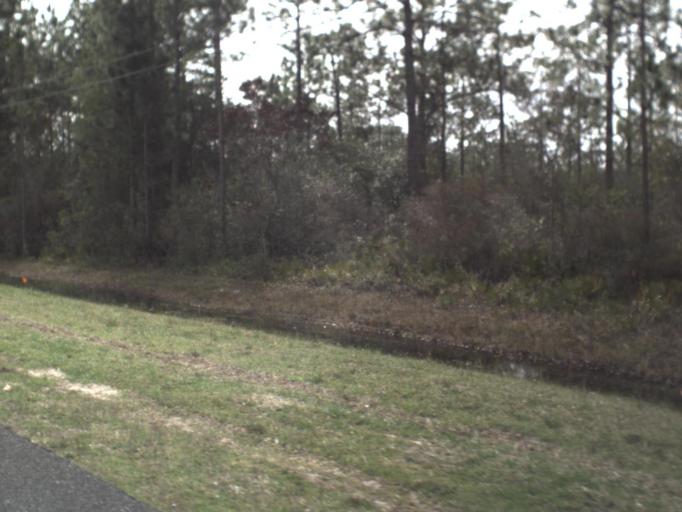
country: US
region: Florida
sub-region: Bay County
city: Youngstown
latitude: 30.4386
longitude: -85.4270
